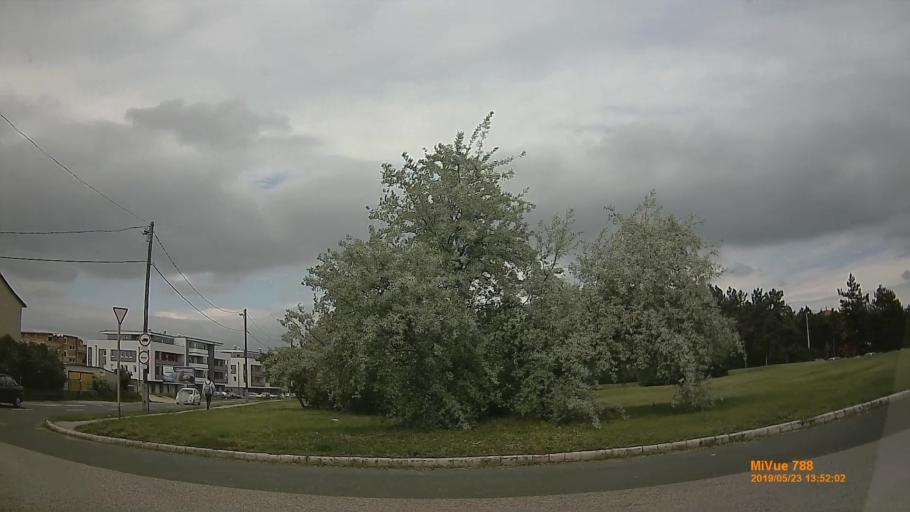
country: HU
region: Veszprem
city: Veszprem
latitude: 47.1060
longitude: 17.9011
